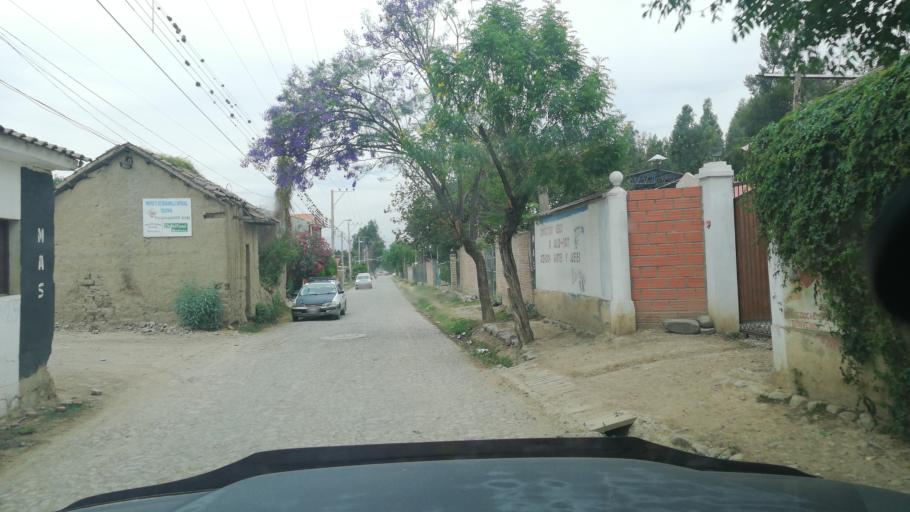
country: BO
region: Cochabamba
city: Cochabamba
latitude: -17.3528
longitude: -66.2196
